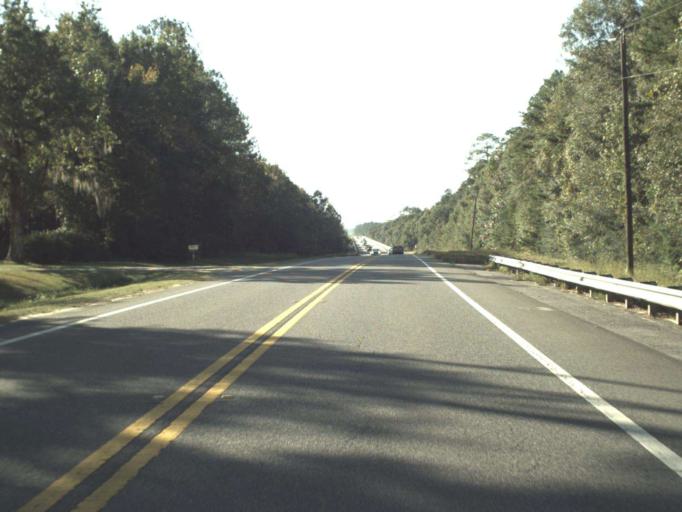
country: US
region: Florida
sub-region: Bay County
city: Laguna Beach
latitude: 30.4474
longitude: -85.8874
